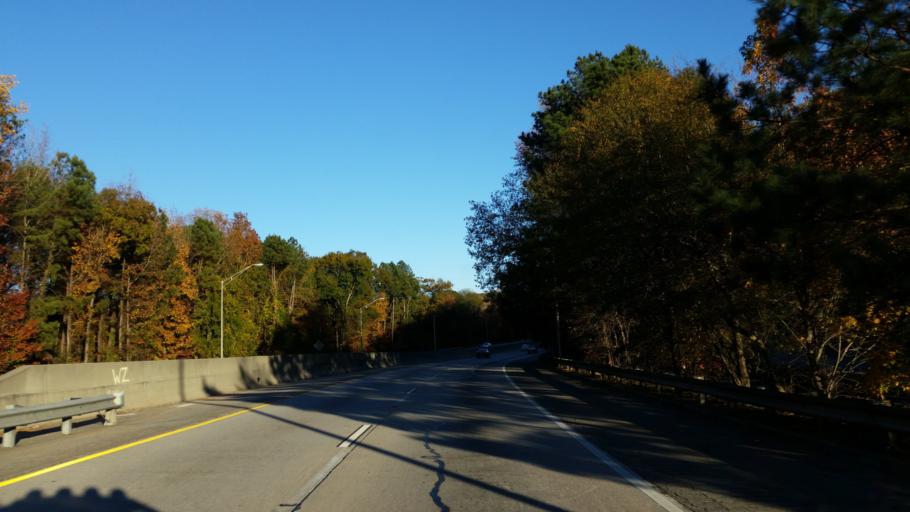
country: US
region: Georgia
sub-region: Fulton County
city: East Point
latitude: 33.6994
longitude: -84.4565
